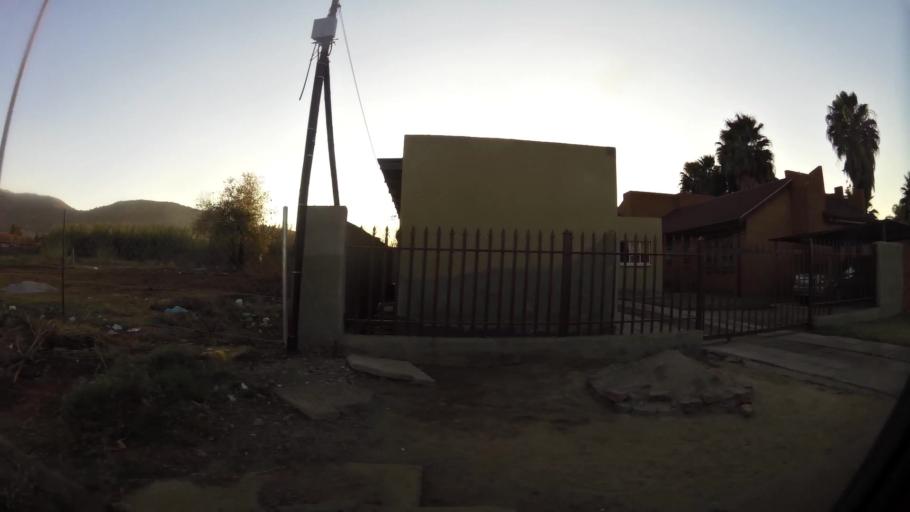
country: ZA
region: North-West
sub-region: Bojanala Platinum District Municipality
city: Rustenburg
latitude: -25.6364
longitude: 27.2048
